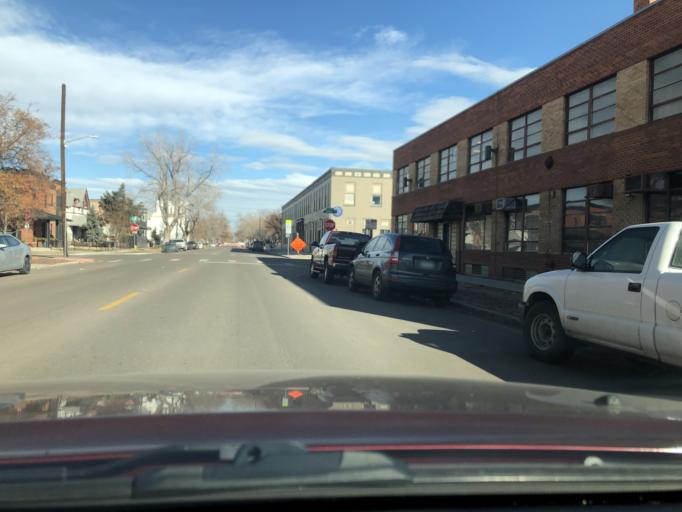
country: US
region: Colorado
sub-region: Denver County
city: Denver
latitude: 39.7553
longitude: -104.9843
